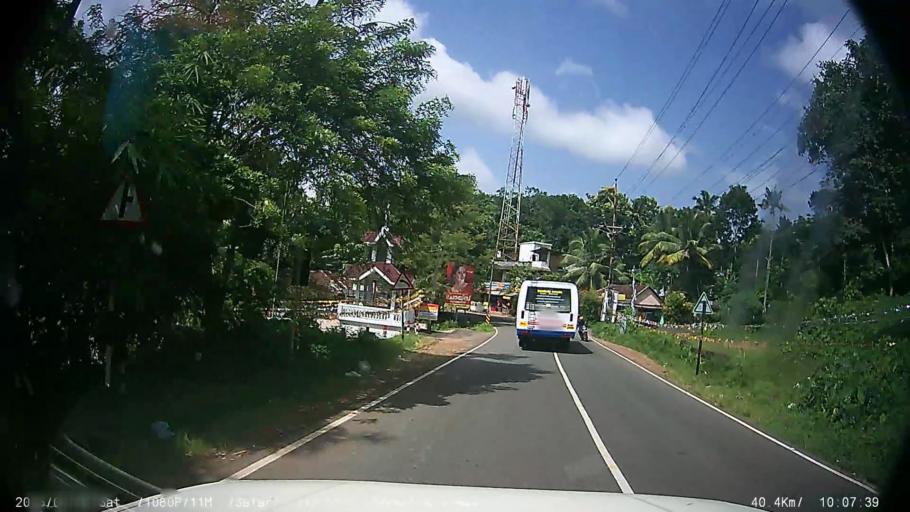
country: IN
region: Kerala
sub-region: Kottayam
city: Changanacheri
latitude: 9.4987
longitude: 76.5727
